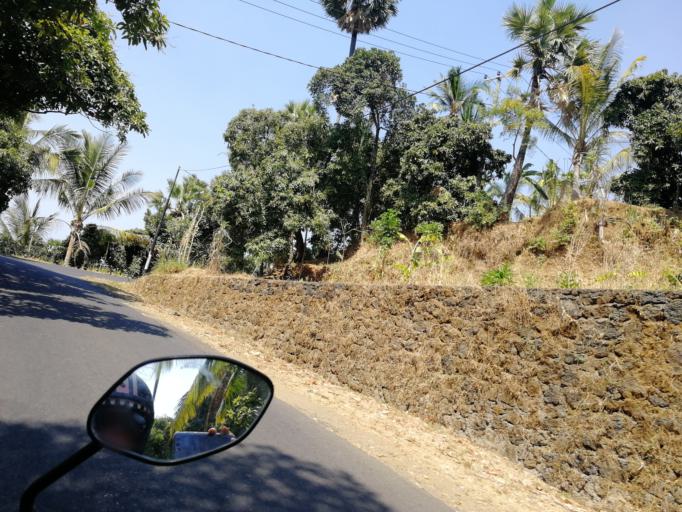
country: ID
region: Bali
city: Banjar Trunyan
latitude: -8.1319
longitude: 115.3237
